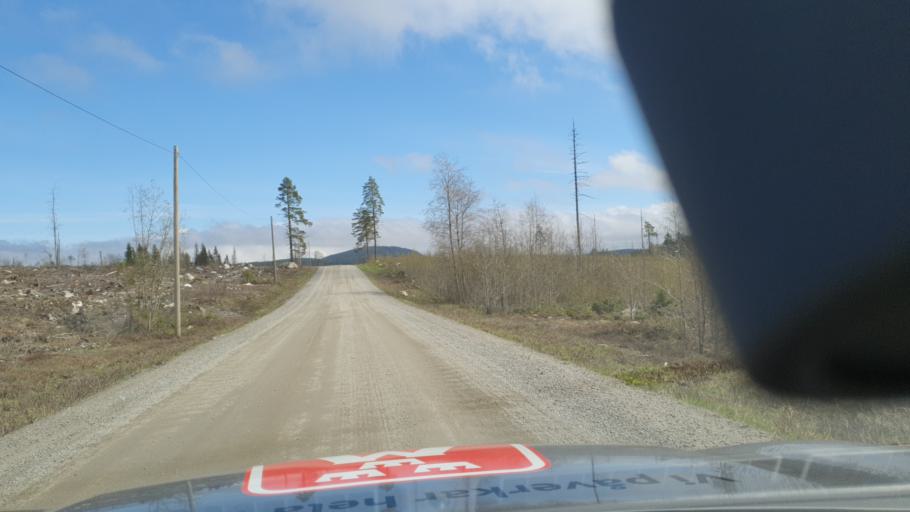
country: SE
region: Vaesterbotten
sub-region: Bjurholms Kommun
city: Bjurholm
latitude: 63.7032
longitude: 18.9151
